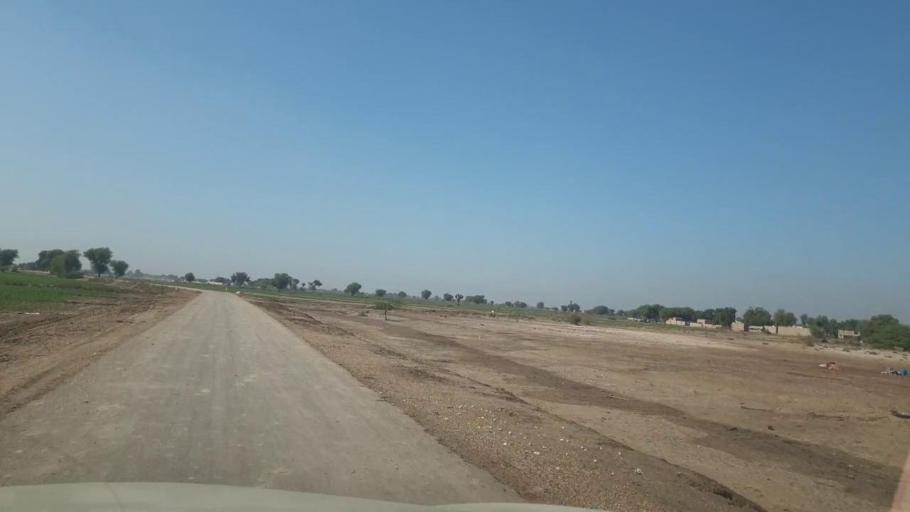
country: PK
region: Sindh
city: Bhan
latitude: 26.5663
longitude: 67.7016
